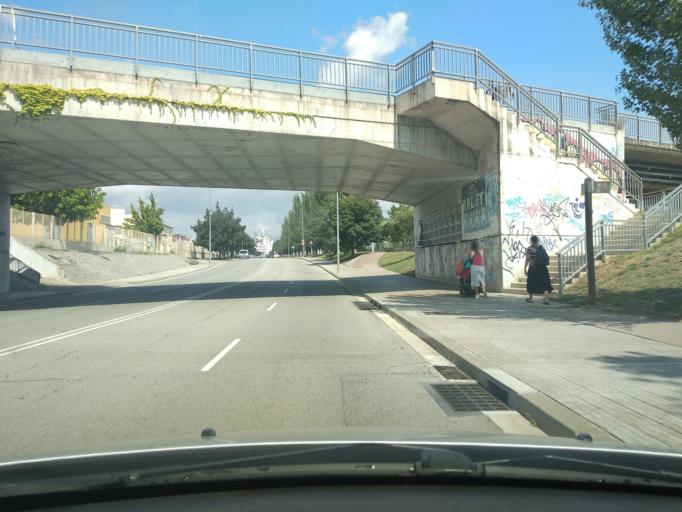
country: ES
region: Catalonia
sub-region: Provincia de Barcelona
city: Granollers
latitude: 41.6015
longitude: 2.2787
